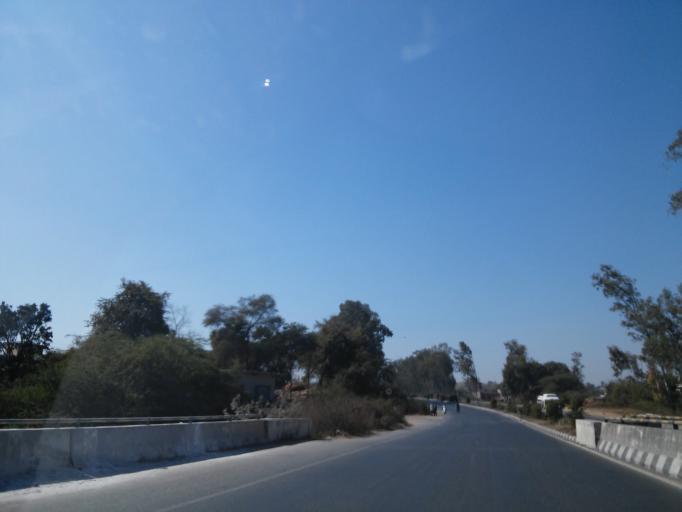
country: IN
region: Rajasthan
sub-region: Dungarpur
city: Dungarpur
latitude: 23.9150
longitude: 73.5590
